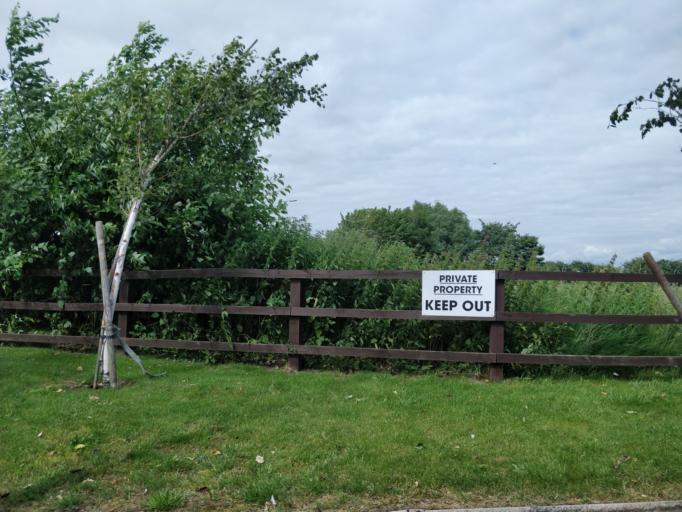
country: GB
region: England
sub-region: Lancashire
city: Banks
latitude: 53.6649
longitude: -2.9531
